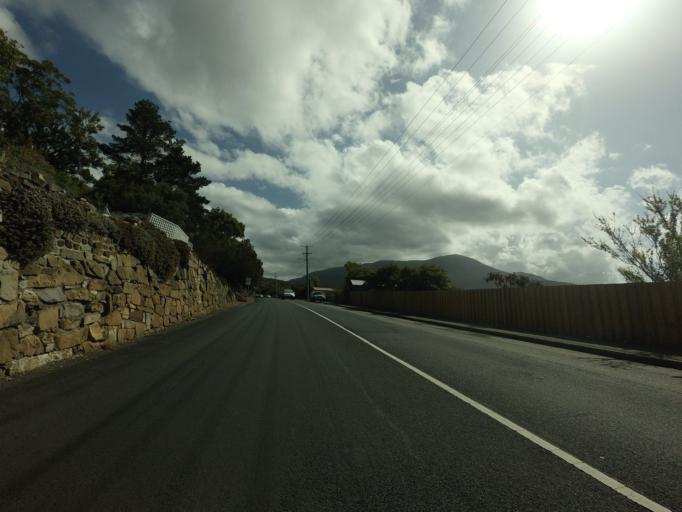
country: AU
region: Tasmania
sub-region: Hobart
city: Dynnyrne
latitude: -42.8982
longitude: 147.3017
